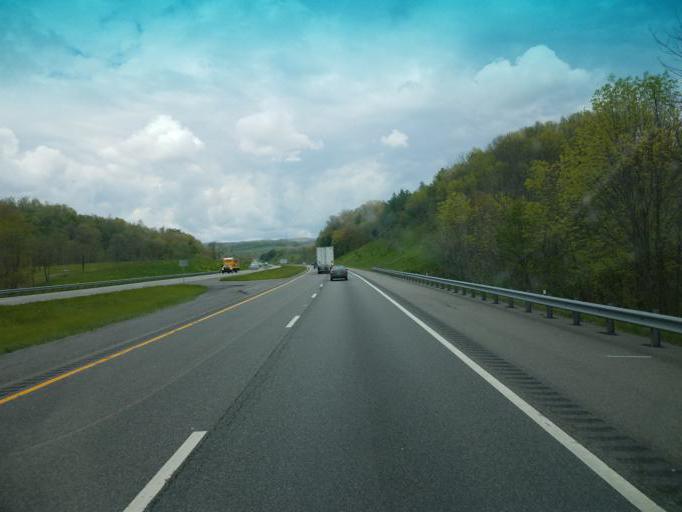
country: US
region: Virginia
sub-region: Wythe County
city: Wytheville
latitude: 36.9964
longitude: -81.0818
